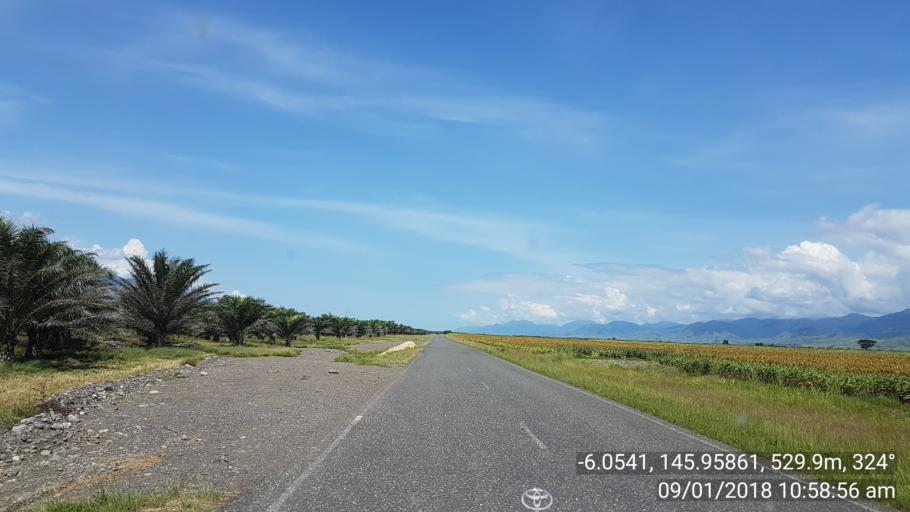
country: PG
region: Eastern Highlands
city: Kainantu
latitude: -6.0542
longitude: 145.9586
